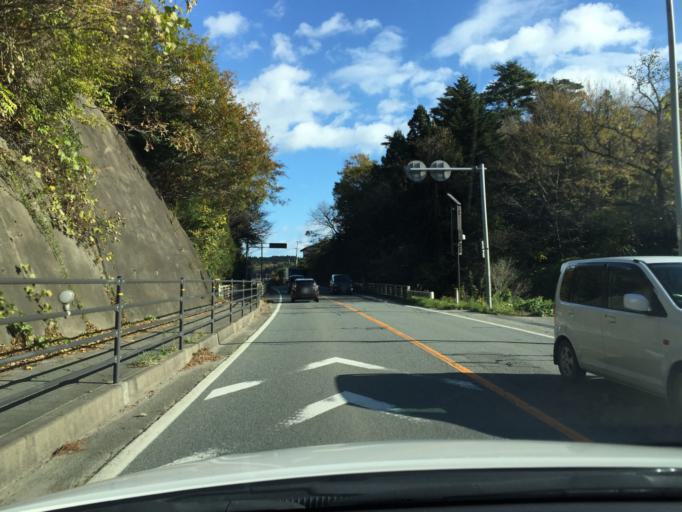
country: JP
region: Fukushima
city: Iwaki
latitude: 37.2161
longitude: 140.9983
